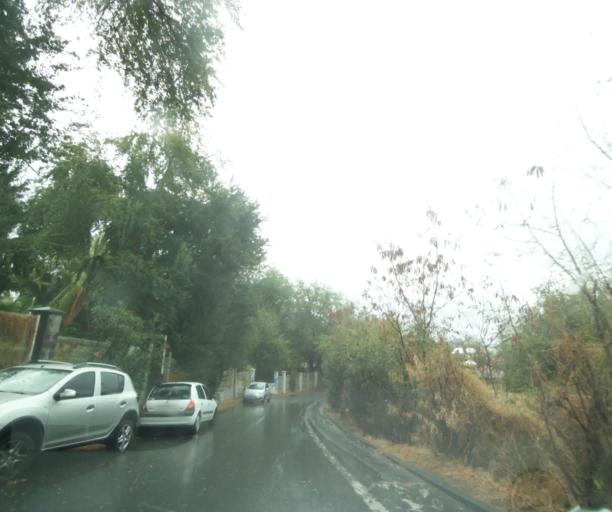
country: RE
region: Reunion
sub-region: Reunion
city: Saint-Paul
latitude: -21.0310
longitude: 55.2272
